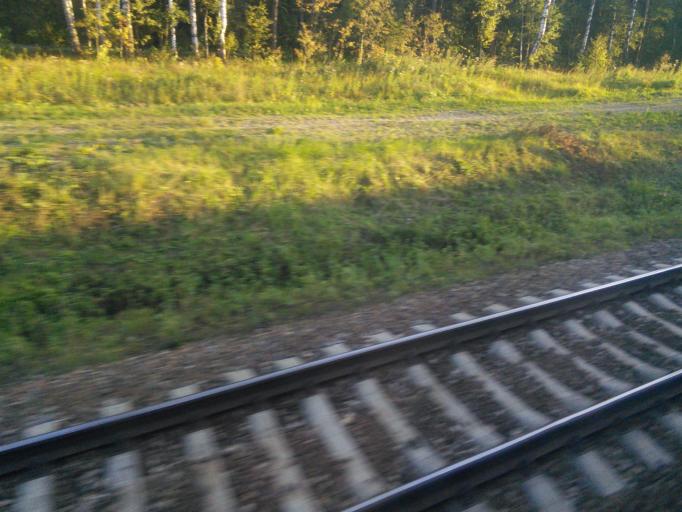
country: RU
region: Moskovskaya
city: Fryazevo
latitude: 55.7200
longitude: 38.4046
